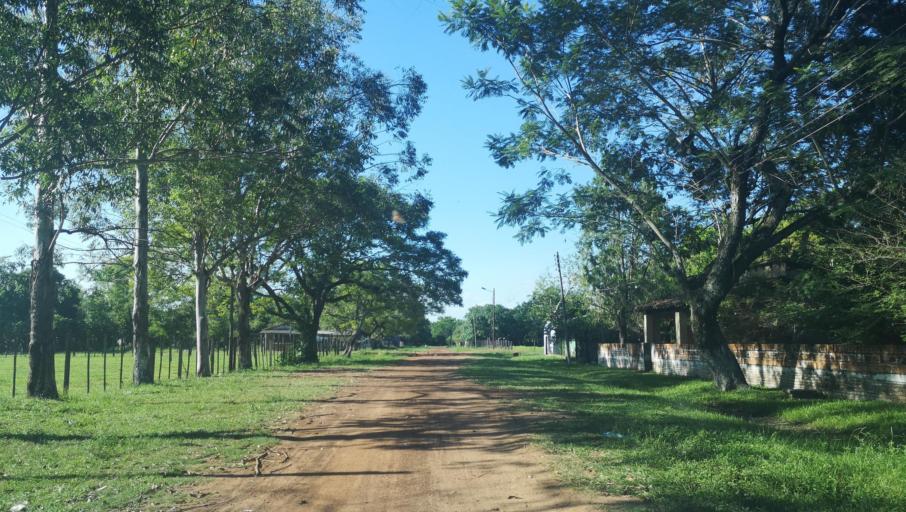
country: PY
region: Caaguazu
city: Carayao
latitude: -25.1944
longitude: -56.4007
